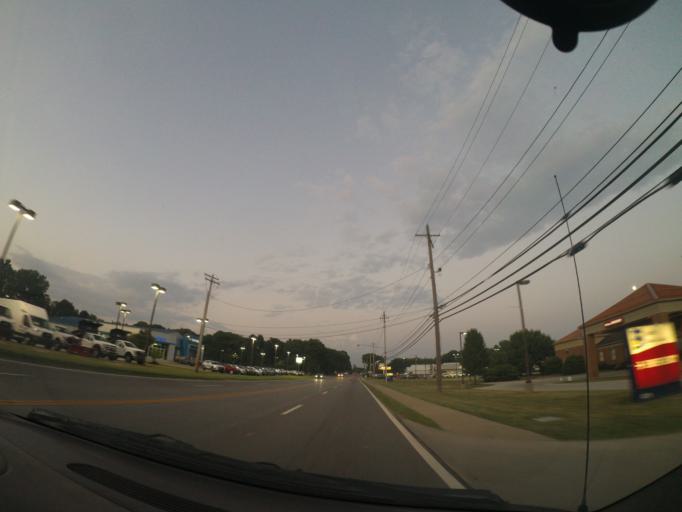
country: US
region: Ohio
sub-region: Lake County
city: North Madison
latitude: 41.8029
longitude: -81.0648
